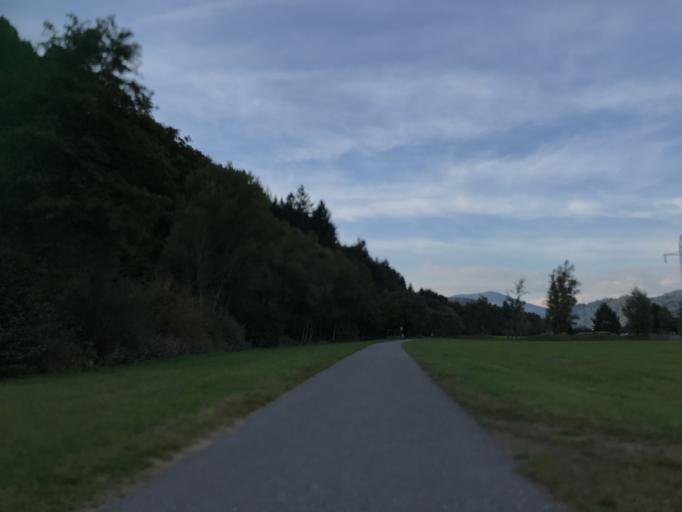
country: DE
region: Baden-Wuerttemberg
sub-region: Freiburg Region
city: Schopfheim
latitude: 47.6569
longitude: 7.8284
